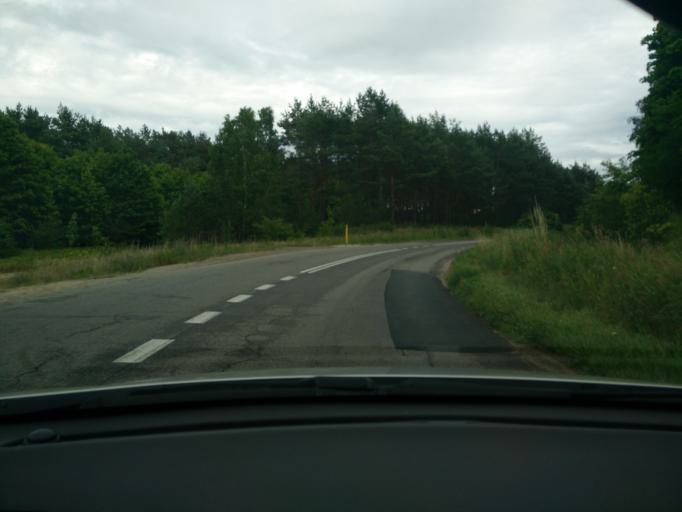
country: PL
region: Pomeranian Voivodeship
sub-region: Powiat pucki
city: Kosakowo
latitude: 54.6034
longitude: 18.4827
